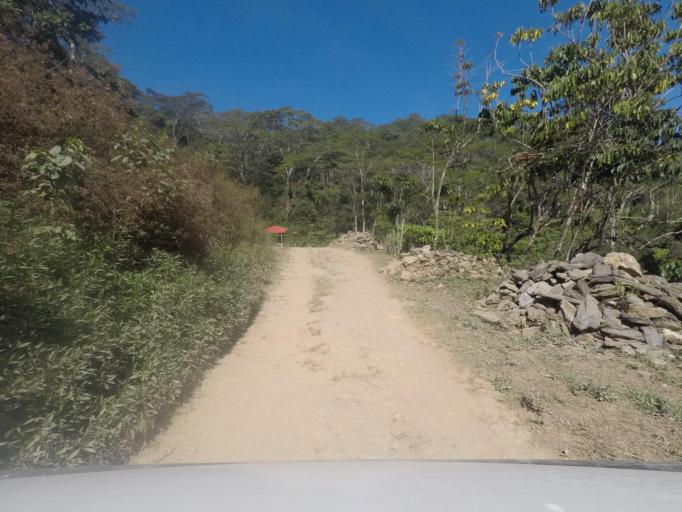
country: TL
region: Ermera
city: Gleno
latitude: -8.7292
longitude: 125.3385
